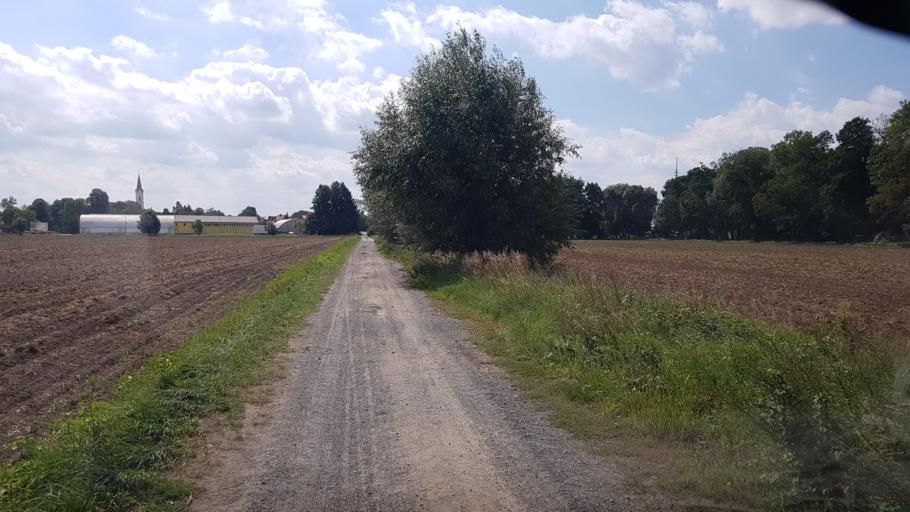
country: DE
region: Brandenburg
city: Lubbenau
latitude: 51.8683
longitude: 13.9281
